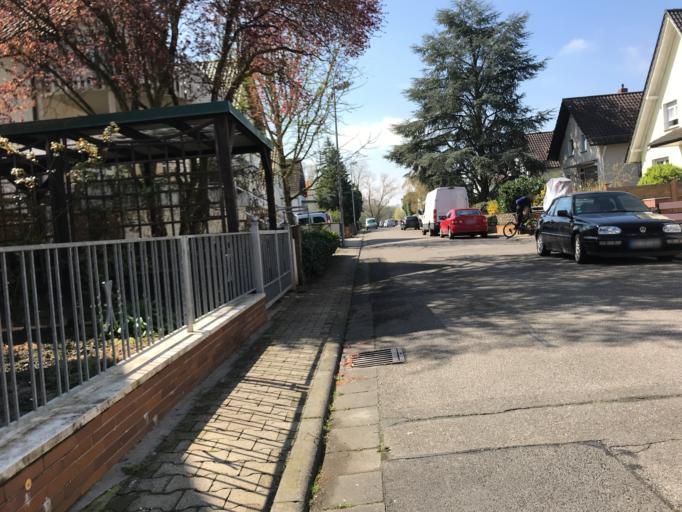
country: DE
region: Rheinland-Pfalz
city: Bodenheim
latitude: 49.9605
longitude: 8.3220
